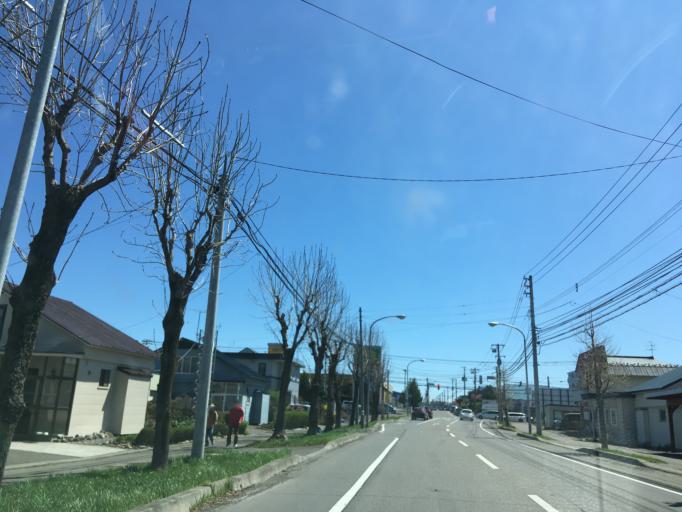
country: JP
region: Hokkaido
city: Obihiro
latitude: 42.9207
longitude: 143.1715
